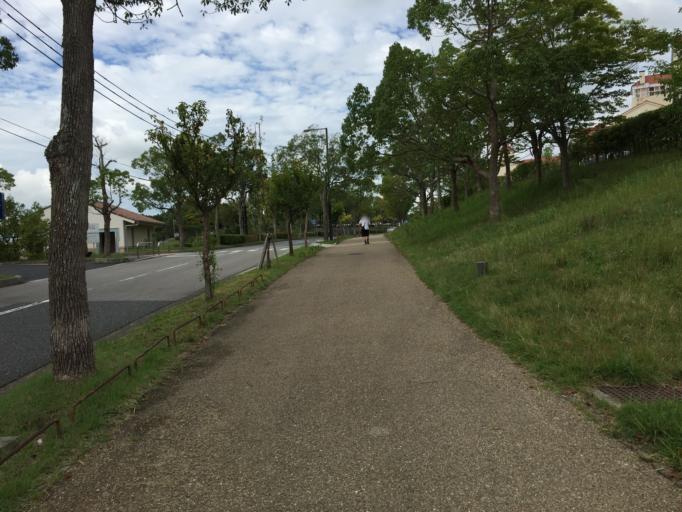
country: JP
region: Hyogo
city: Kobe
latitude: 34.7054
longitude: 135.1126
